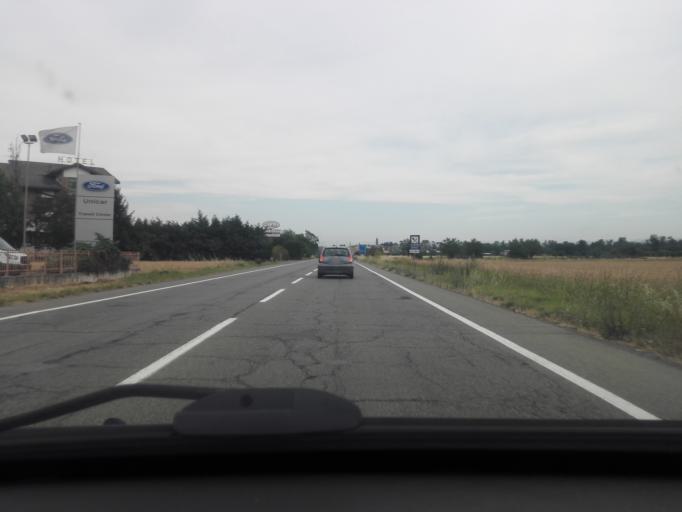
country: IT
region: Piedmont
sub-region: Provincia di Alessandria
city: Pozzolo Formigaro
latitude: 44.8033
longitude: 8.7732
